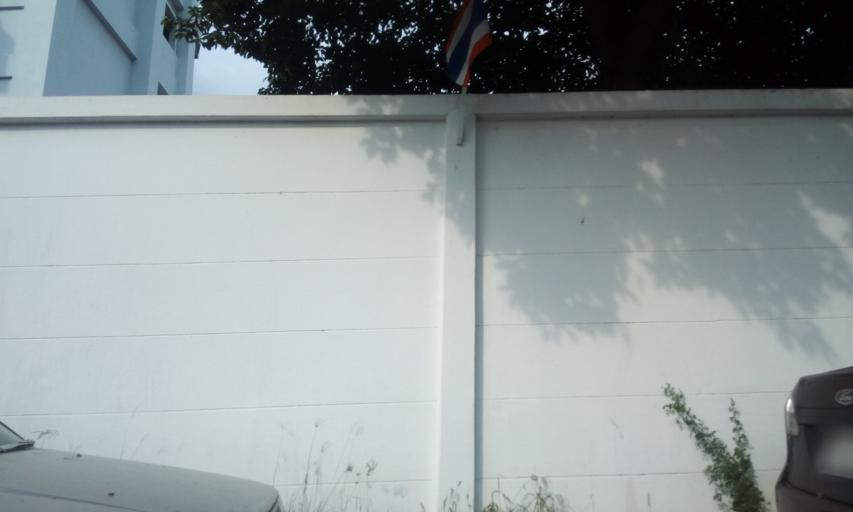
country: TH
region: Bangkok
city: Don Mueang
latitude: 13.9127
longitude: 100.5567
